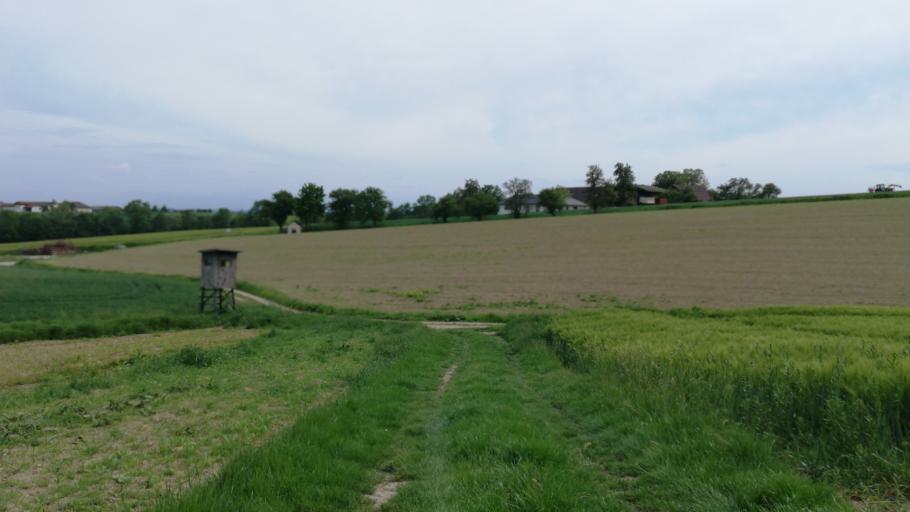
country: AT
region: Upper Austria
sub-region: Wels-Land
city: Gunskirchen
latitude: 48.1692
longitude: 13.9426
